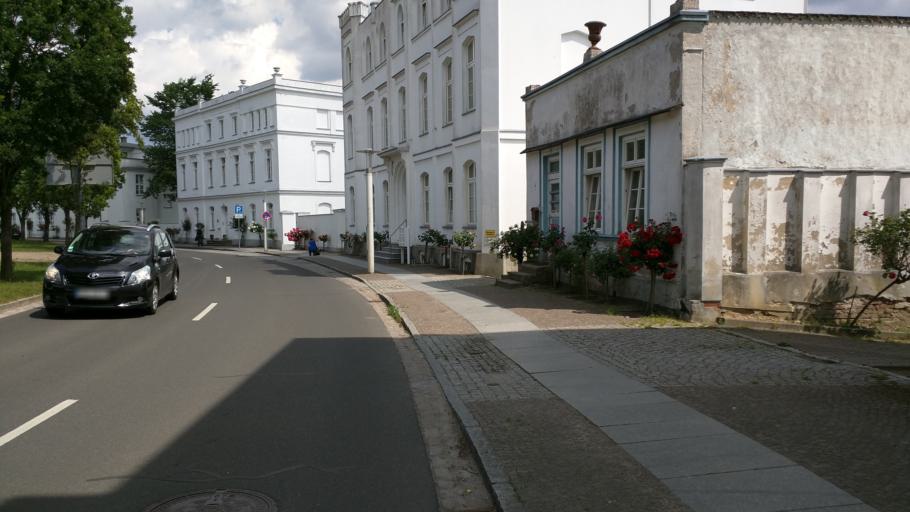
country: DE
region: Mecklenburg-Vorpommern
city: Putbus
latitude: 54.3540
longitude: 13.4762
